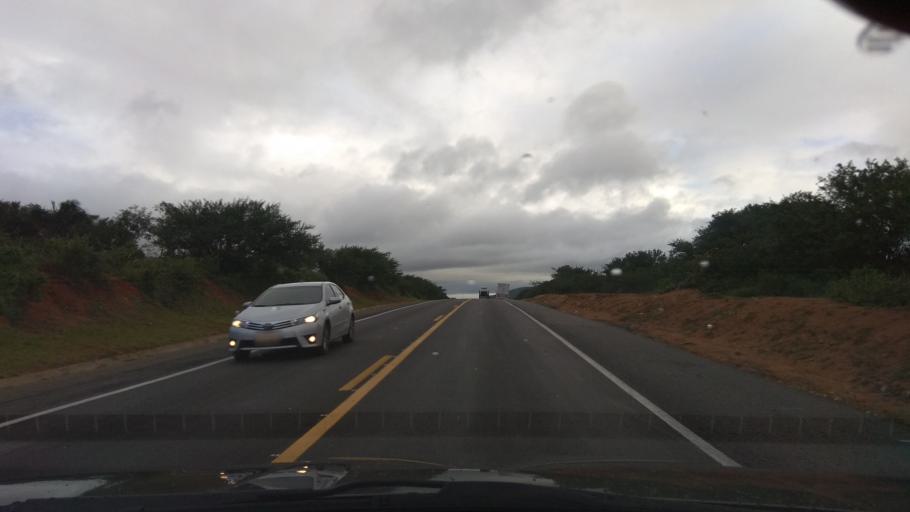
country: BR
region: Bahia
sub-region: Santa Ines
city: Santa Ines
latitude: -13.2849
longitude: -40.0198
